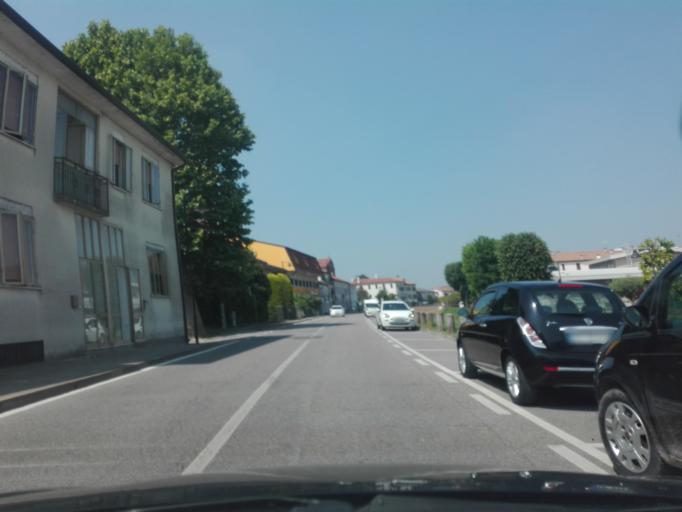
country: IT
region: Veneto
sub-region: Provincia di Rovigo
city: Villadose
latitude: 45.0722
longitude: 11.8933
